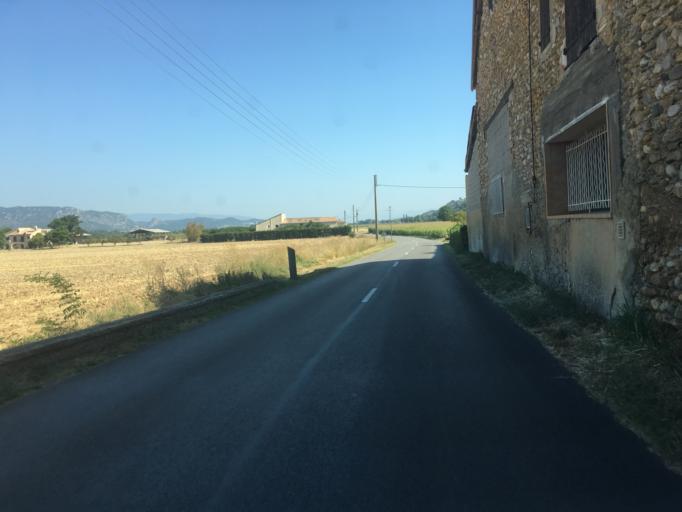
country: FR
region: Provence-Alpes-Cote d'Azur
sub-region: Departement des Alpes-de-Haute-Provence
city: Manosque
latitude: 43.8059
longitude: 5.8419
